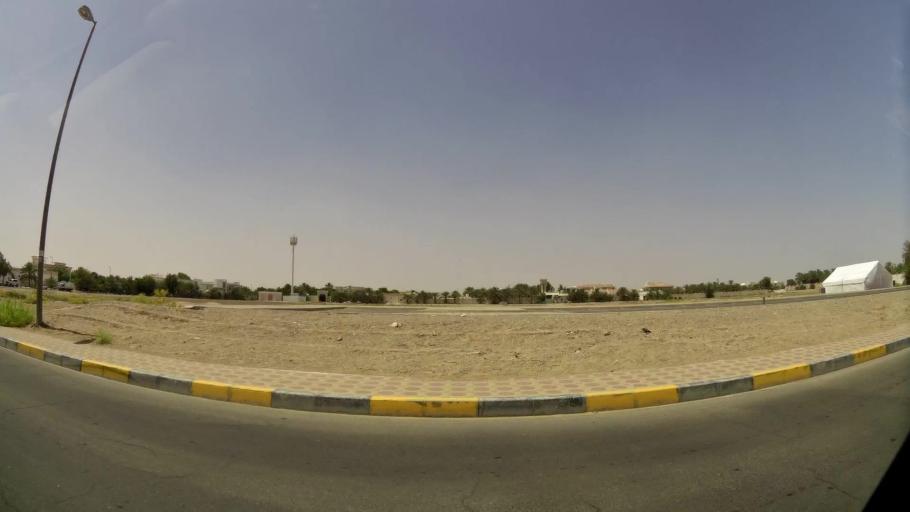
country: AE
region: Abu Dhabi
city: Al Ain
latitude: 24.2480
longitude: 55.7040
